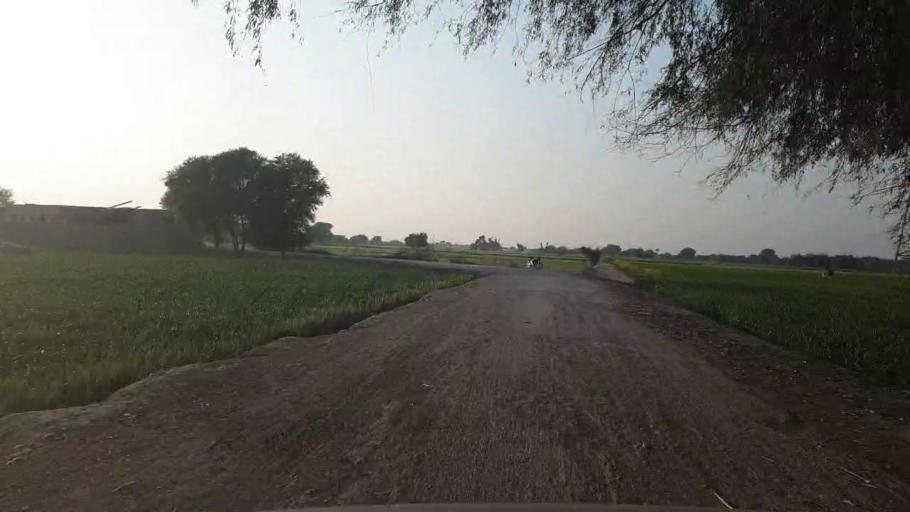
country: PK
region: Sindh
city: Hala
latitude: 25.8705
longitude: 68.4062
